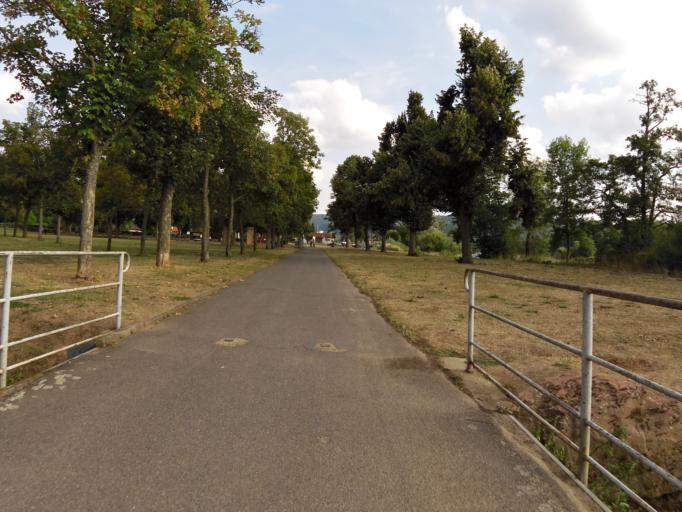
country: DE
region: Bavaria
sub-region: Regierungsbezirk Unterfranken
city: Grossheubach
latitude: 49.7249
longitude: 9.2188
